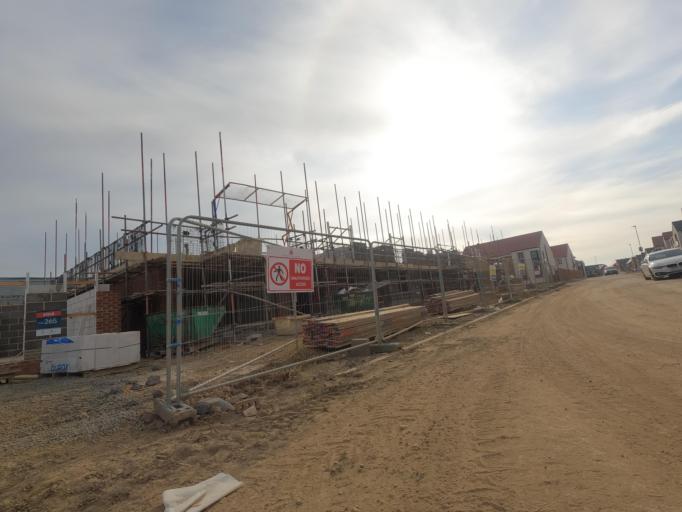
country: GB
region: England
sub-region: Newcastle upon Tyne
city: Hazlerigg
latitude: 55.0309
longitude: -1.6569
